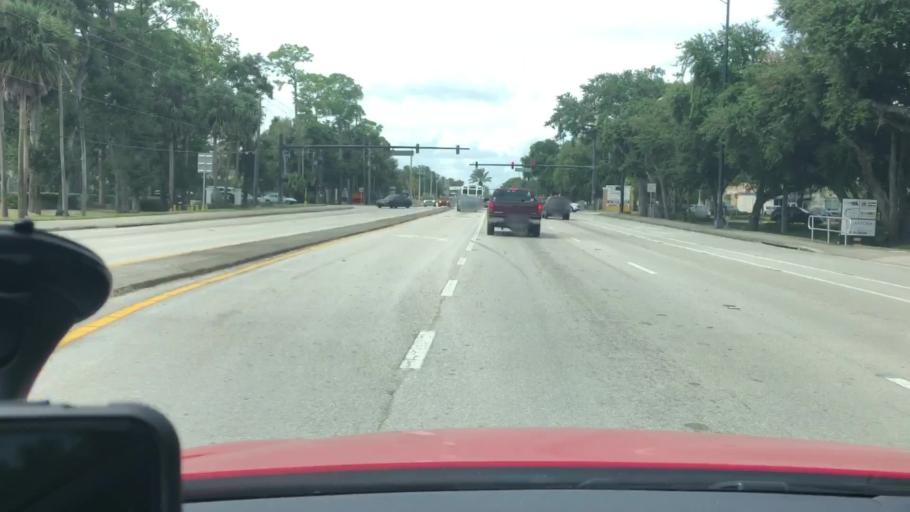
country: US
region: Florida
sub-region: Volusia County
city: Port Orange
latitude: 29.1238
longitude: -81.0030
